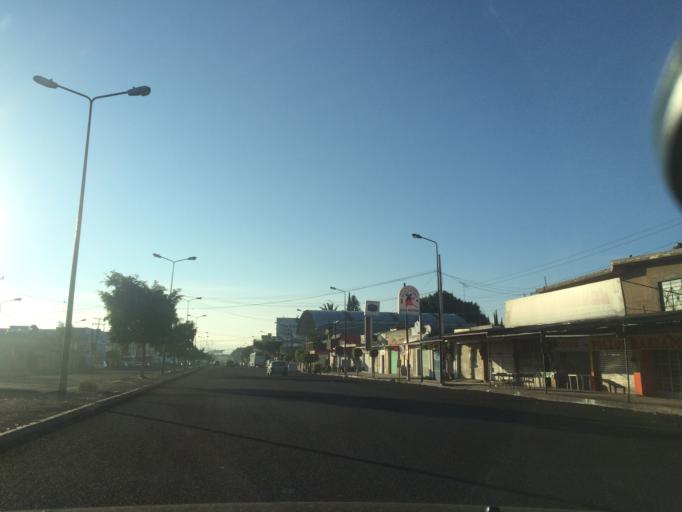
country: MX
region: Puebla
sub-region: Santiago Miahuatlan
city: San Jose Monte Chiquito
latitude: 18.4754
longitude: -97.4351
